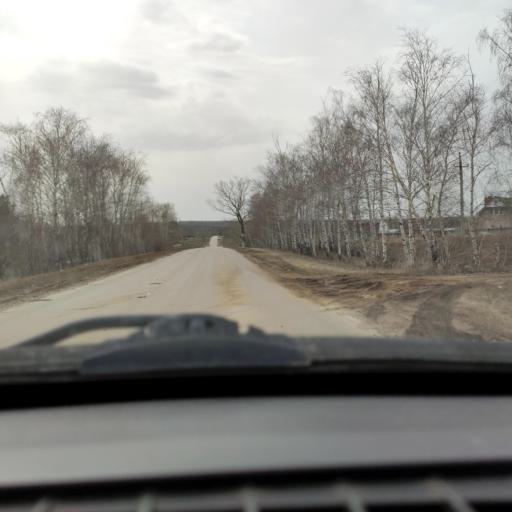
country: RU
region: Samara
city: Dubovyy Umet
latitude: 53.0439
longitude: 50.1809
